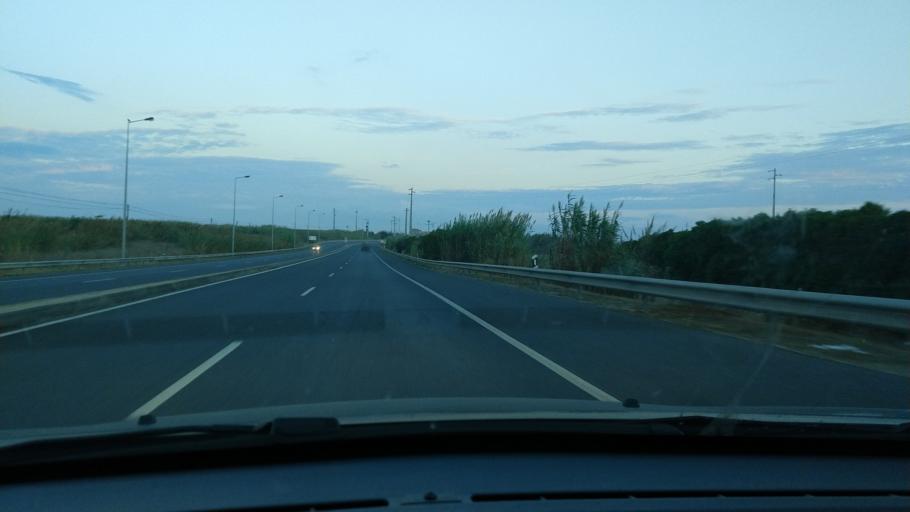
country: PT
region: Leiria
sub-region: Peniche
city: Atouguia da Baleia
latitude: 39.3475
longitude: -9.3475
